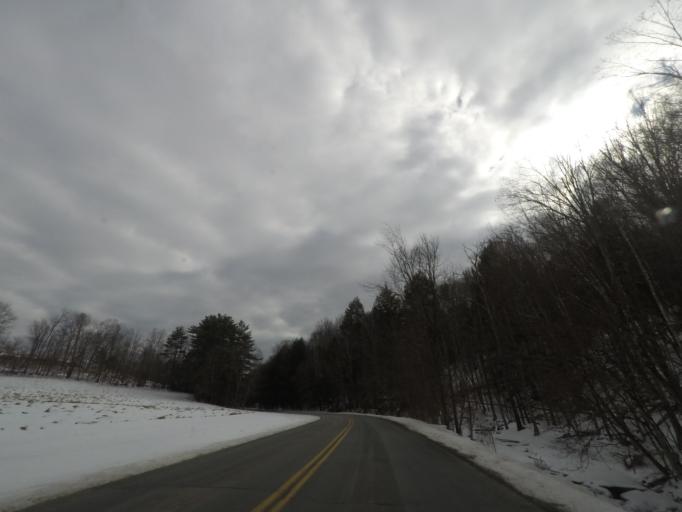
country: US
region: New York
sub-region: Rensselaer County
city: Hoosick Falls
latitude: 42.8821
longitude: -73.4165
